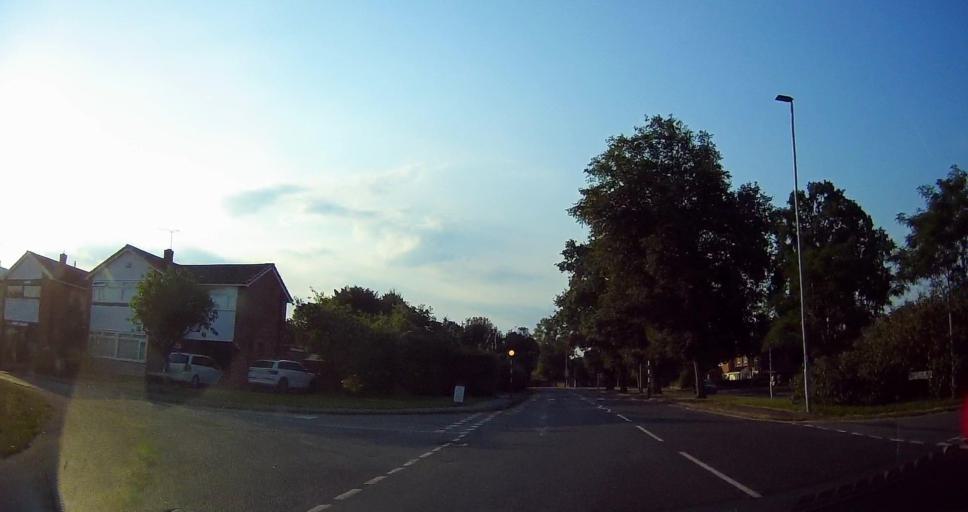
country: GB
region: England
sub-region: Cheshire East
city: Nantwich
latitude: 53.0586
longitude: -2.5180
